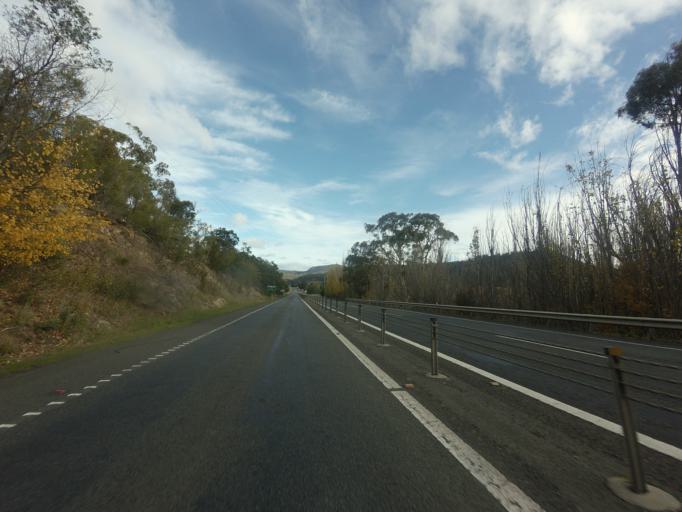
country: AU
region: Tasmania
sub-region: Brighton
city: Bridgewater
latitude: -42.5894
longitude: 147.2239
